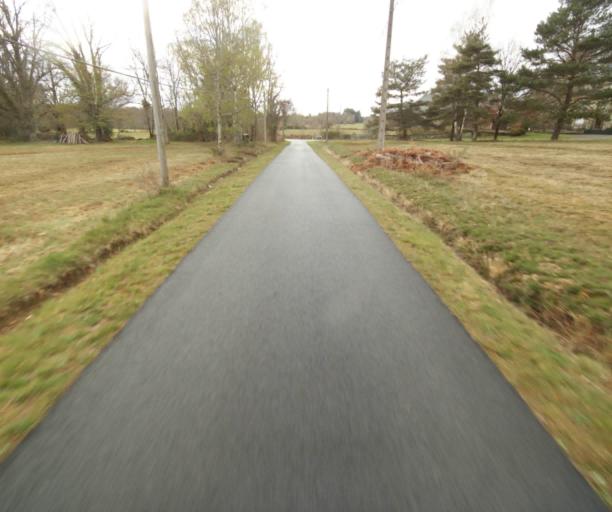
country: FR
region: Limousin
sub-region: Departement de la Correze
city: Saint-Privat
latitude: 45.2194
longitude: 2.0199
